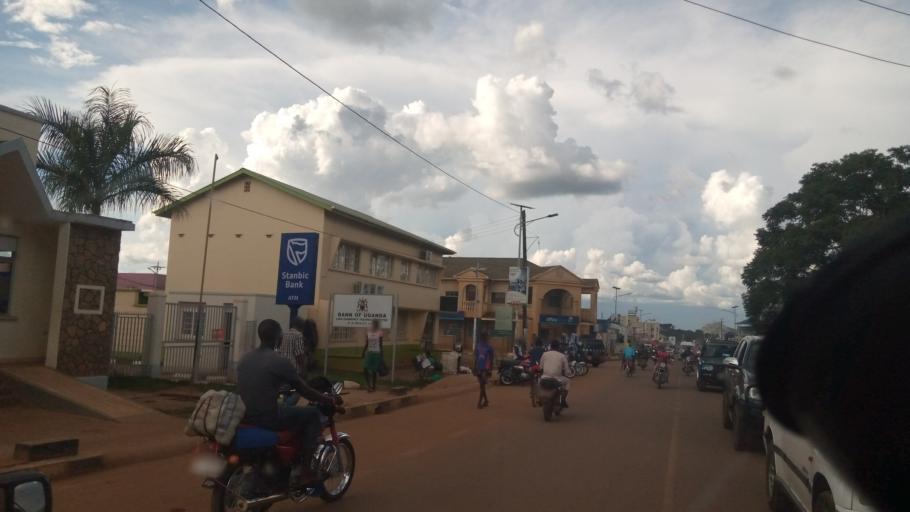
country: UG
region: Northern Region
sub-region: Lira District
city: Lira
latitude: 2.2390
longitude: 32.8945
